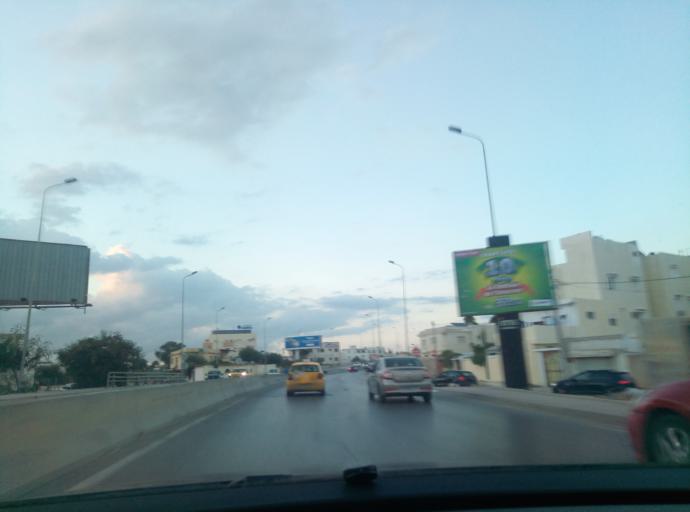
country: TN
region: Manouba
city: Manouba
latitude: 36.8073
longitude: 10.1187
